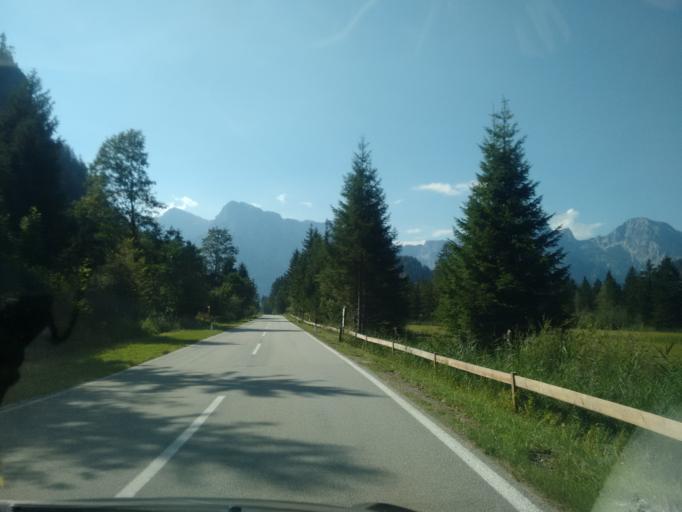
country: AT
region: Upper Austria
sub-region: Politischer Bezirk Gmunden
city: Gruenau im Almtal
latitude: 47.7726
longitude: 13.9572
